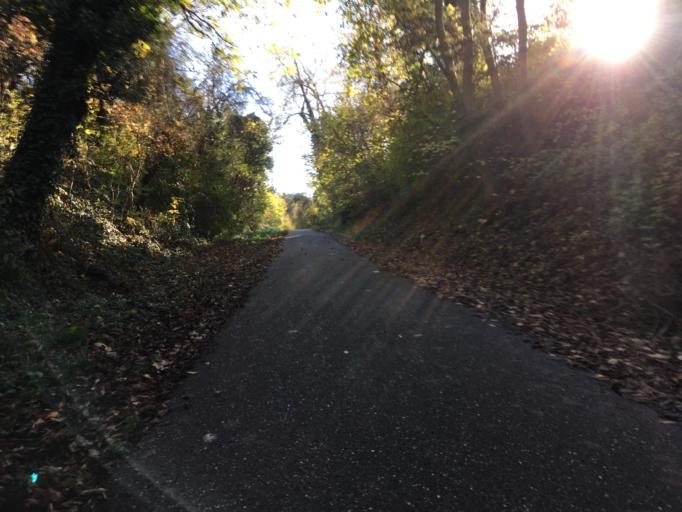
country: DE
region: Baden-Wuerttemberg
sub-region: Karlsruhe Region
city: Oberderdingen
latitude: 49.0577
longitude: 8.8041
